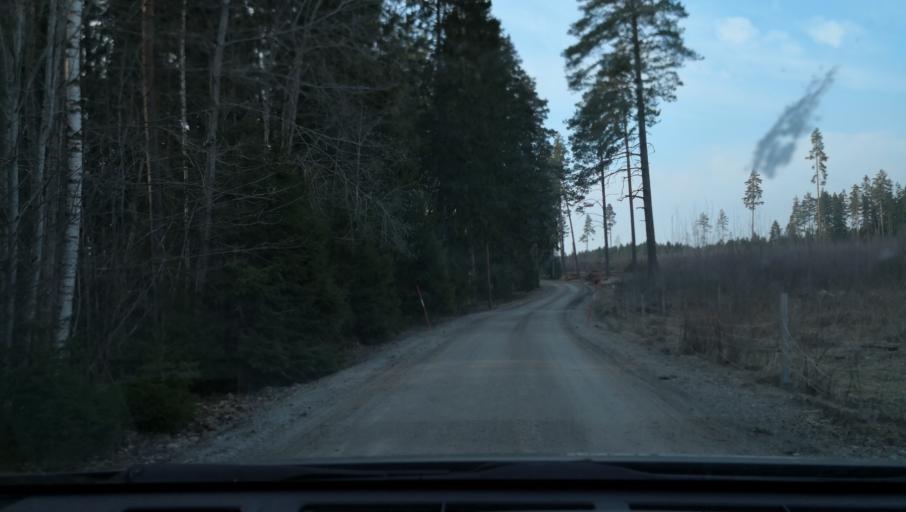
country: SE
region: OErebro
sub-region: Lindesbergs Kommun
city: Frovi
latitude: 59.3516
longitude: 15.3415
